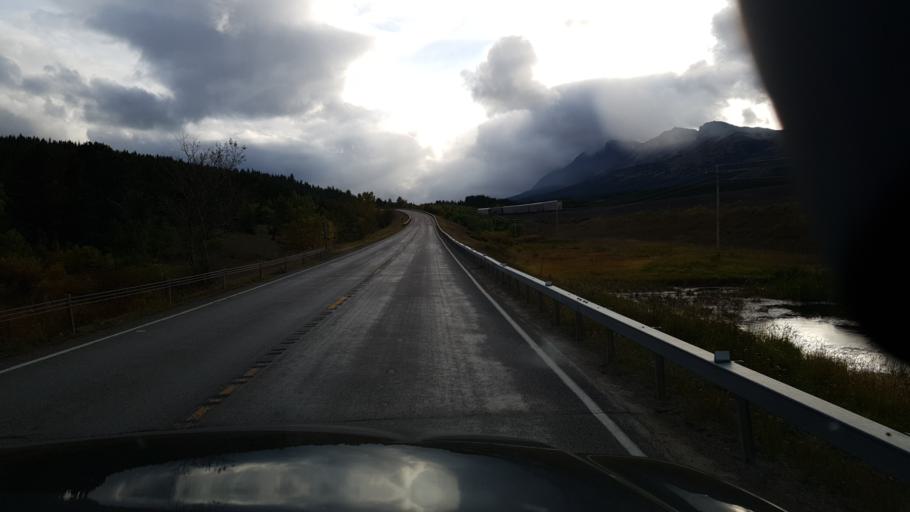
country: US
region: Montana
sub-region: Glacier County
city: South Browning
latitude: 48.3858
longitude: -113.2674
